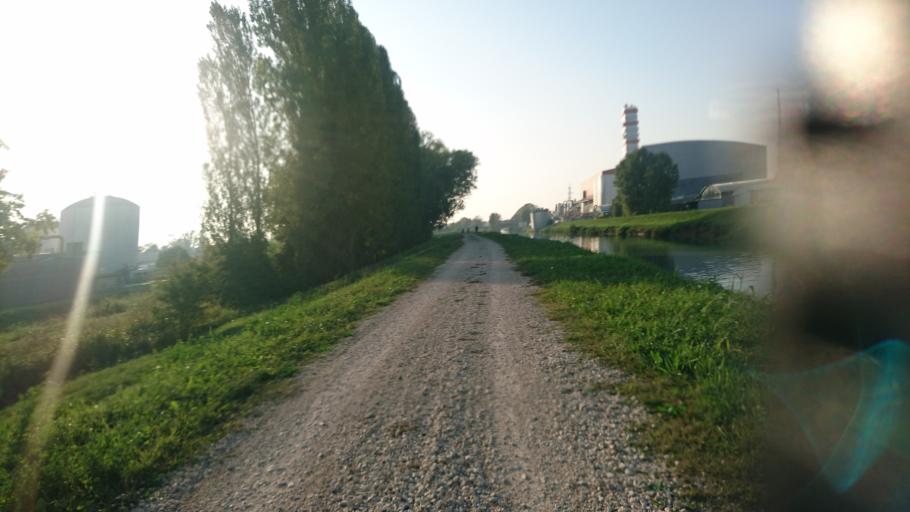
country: IT
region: Veneto
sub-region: Provincia di Padova
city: Noventa
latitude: 45.4055
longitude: 11.9283
